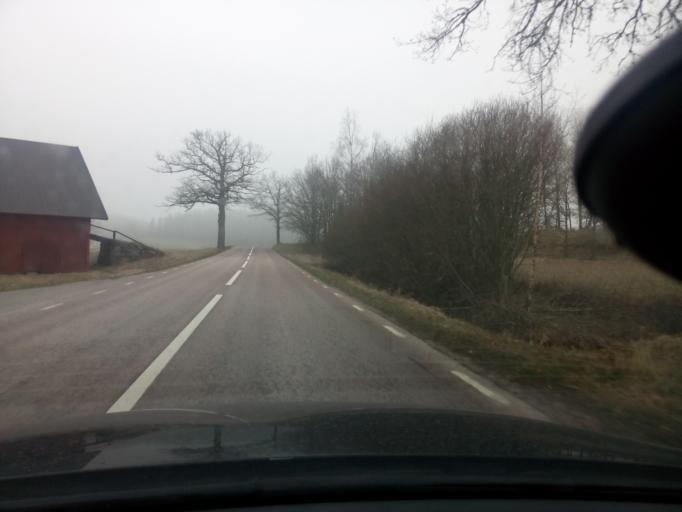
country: SE
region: Soedermanland
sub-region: Nykopings Kommun
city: Nykoping
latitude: 58.8880
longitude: 17.0880
